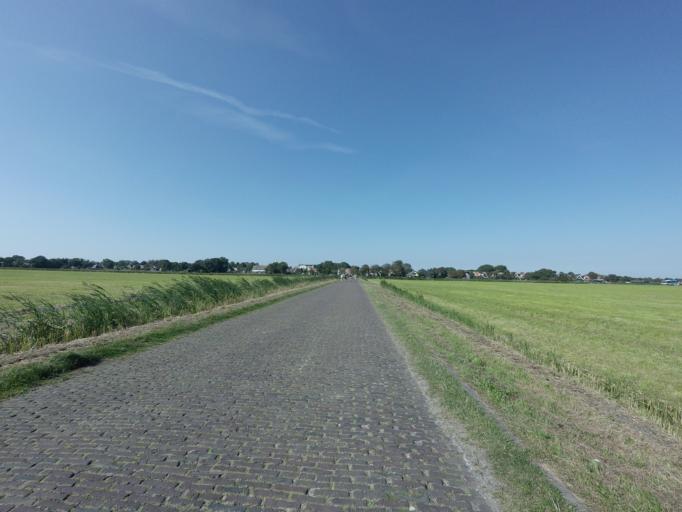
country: NL
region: Friesland
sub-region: Gemeente Schiermonnikoog
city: Schiermonnikoog
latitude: 53.4741
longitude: 6.1616
